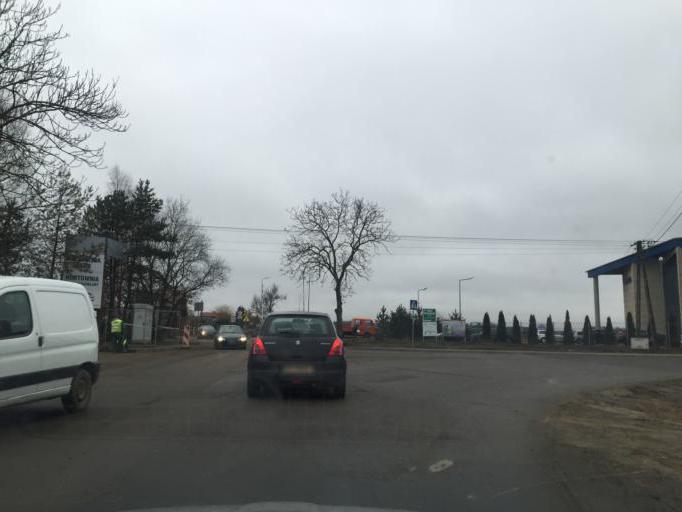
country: PL
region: Pomeranian Voivodeship
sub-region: Powiat kartuski
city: Chwaszczyno
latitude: 54.4181
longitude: 18.4504
